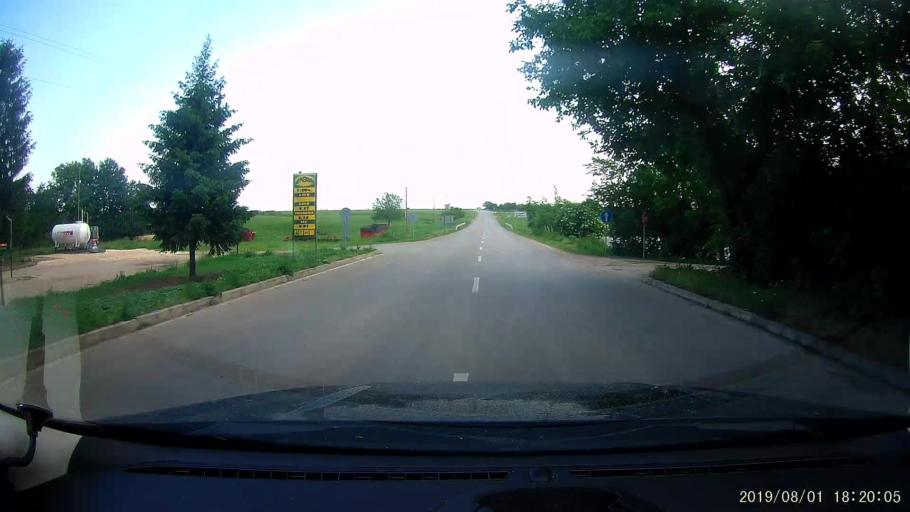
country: BG
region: Shumen
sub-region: Obshtina Kaolinovo
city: Kaolinovo
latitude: 43.6779
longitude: 27.0903
